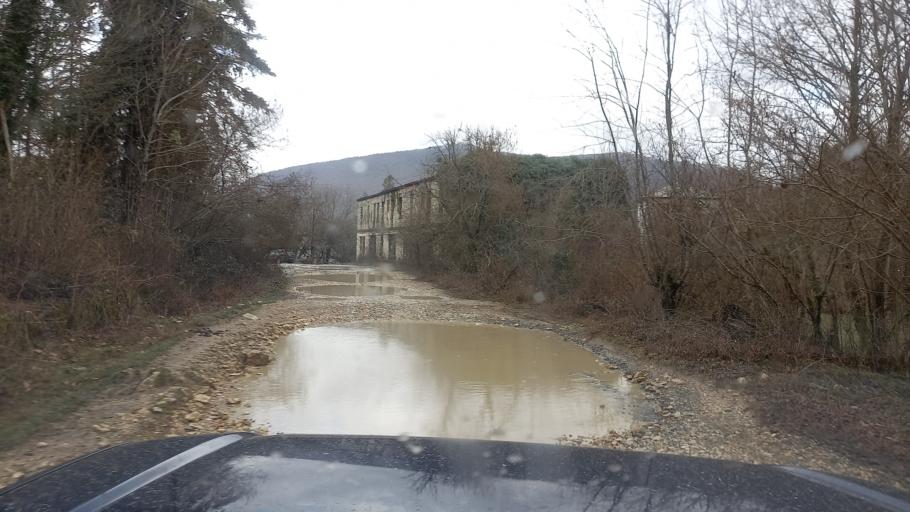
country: GE
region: Abkhazia
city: Dranda
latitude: 43.0347
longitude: 41.3239
